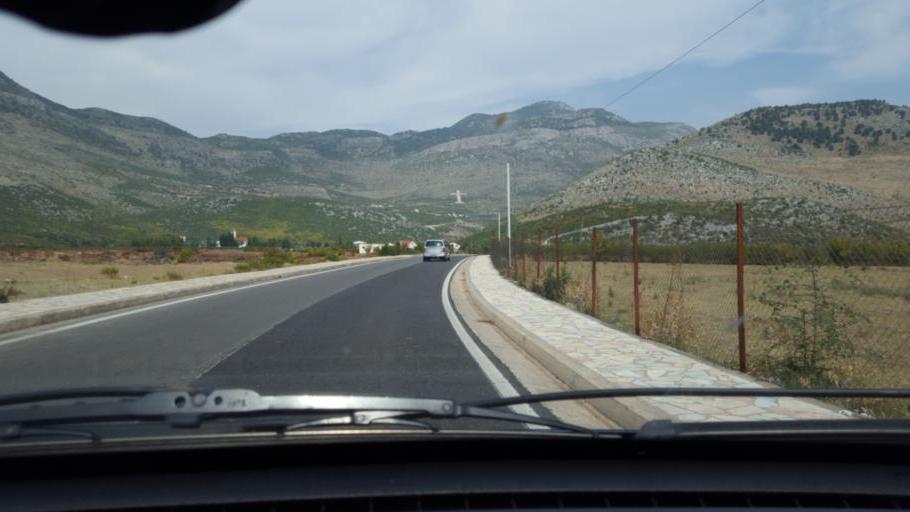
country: AL
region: Shkoder
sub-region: Rrethi i Malesia e Madhe
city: Hot
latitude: 42.3536
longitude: 19.4421
